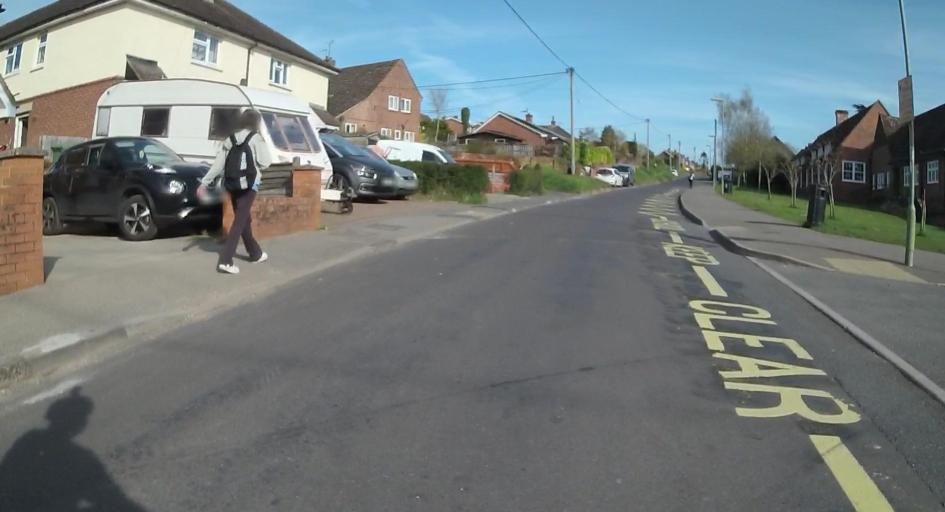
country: GB
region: England
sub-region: Hampshire
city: Overton
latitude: 51.2263
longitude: -1.3362
